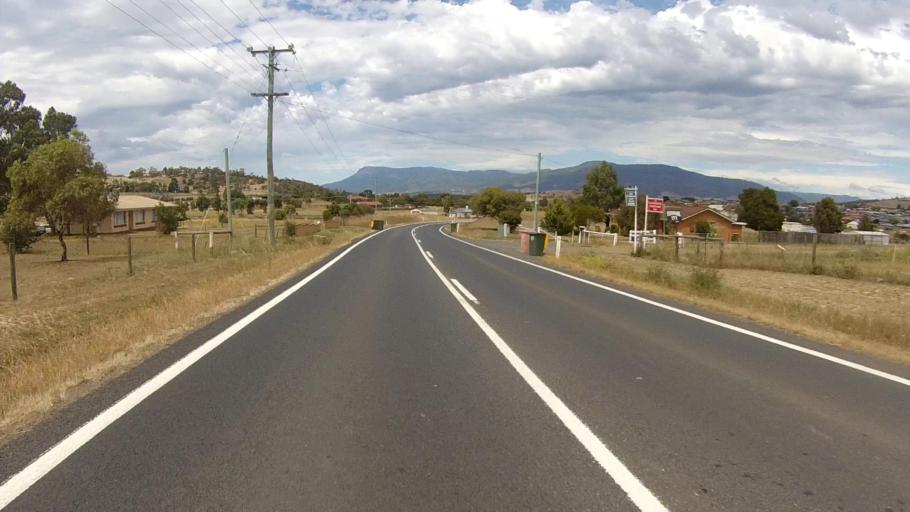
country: AU
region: Tasmania
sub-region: Brighton
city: Bridgewater
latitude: -42.6987
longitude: 147.2692
